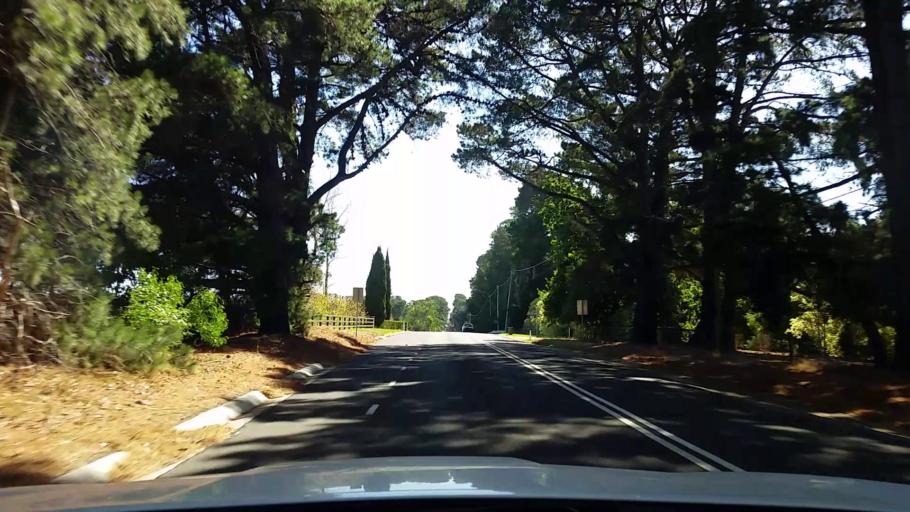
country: AU
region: Victoria
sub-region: Mornington Peninsula
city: Hastings
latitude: -38.3115
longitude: 145.1457
